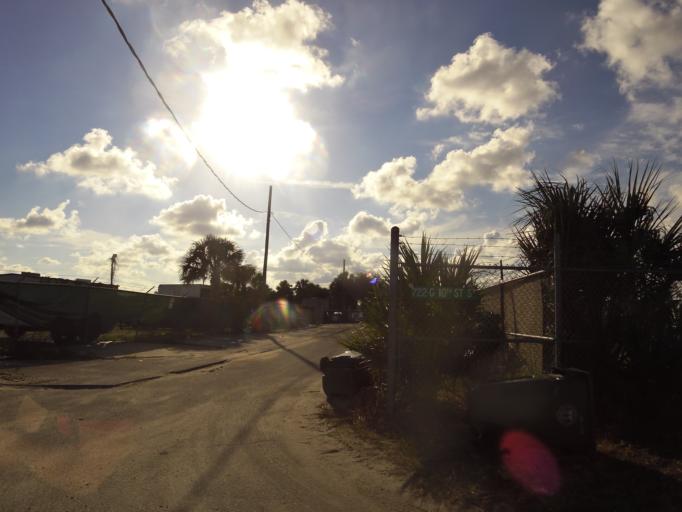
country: US
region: Florida
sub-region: Duval County
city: Jacksonville Beach
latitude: 30.2806
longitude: -81.3982
